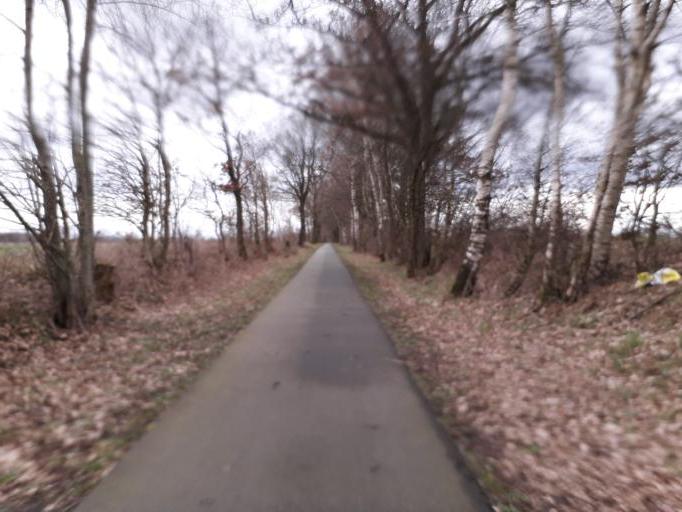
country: DE
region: Schleswig-Holstein
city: Stapelfeld
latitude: 53.5720
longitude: 10.2244
